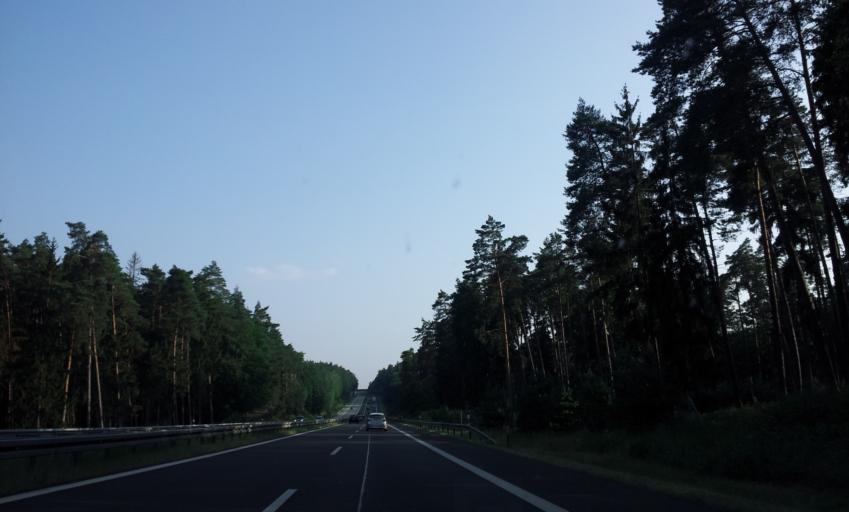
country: DE
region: Brandenburg
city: Althuttendorf
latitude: 53.0558
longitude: 13.8380
